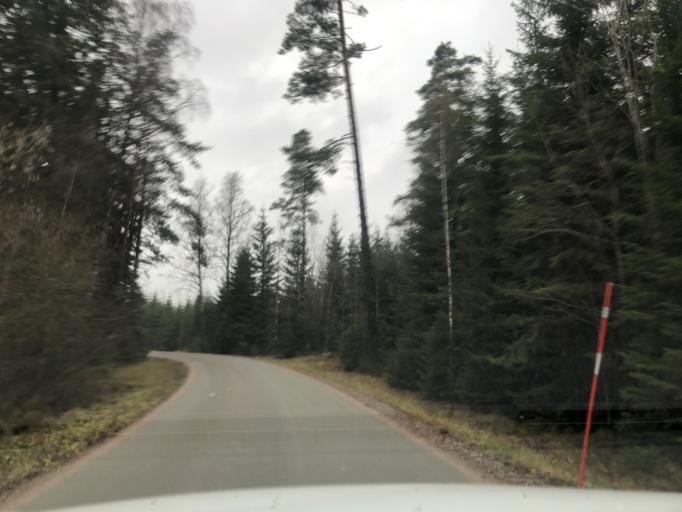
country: SE
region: Vaestra Goetaland
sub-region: Ulricehamns Kommun
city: Ulricehamn
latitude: 57.8552
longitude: 13.6282
